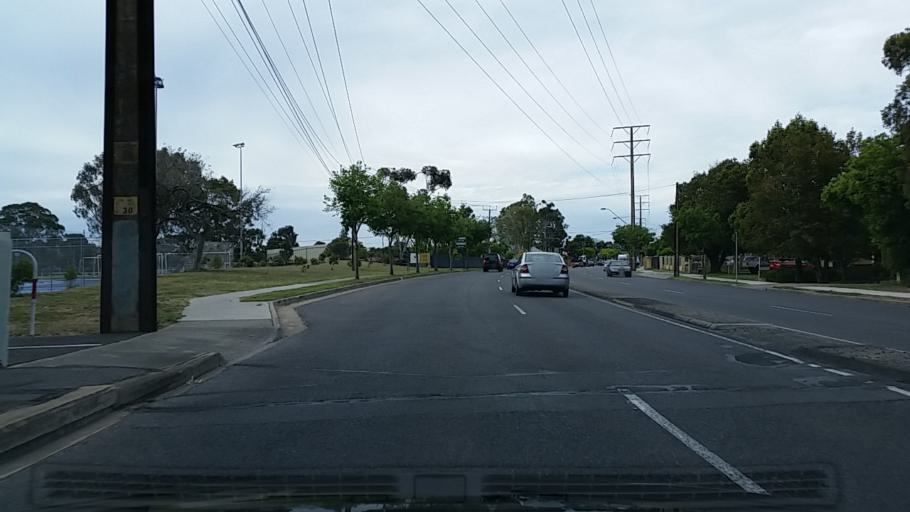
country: AU
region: South Australia
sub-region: Charles Sturt
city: Allenby Gardens
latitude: -34.9135
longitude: 138.5481
